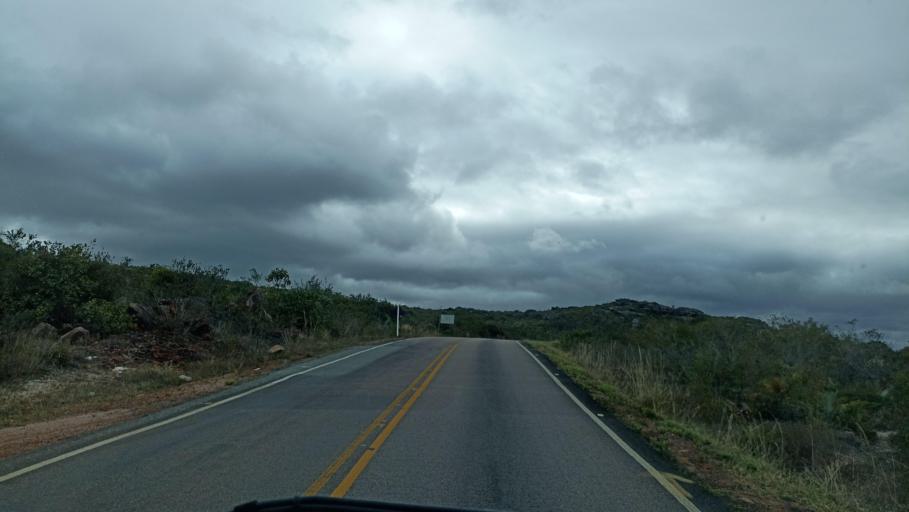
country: BR
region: Bahia
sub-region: Andarai
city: Vera Cruz
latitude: -12.9928
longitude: -41.3539
